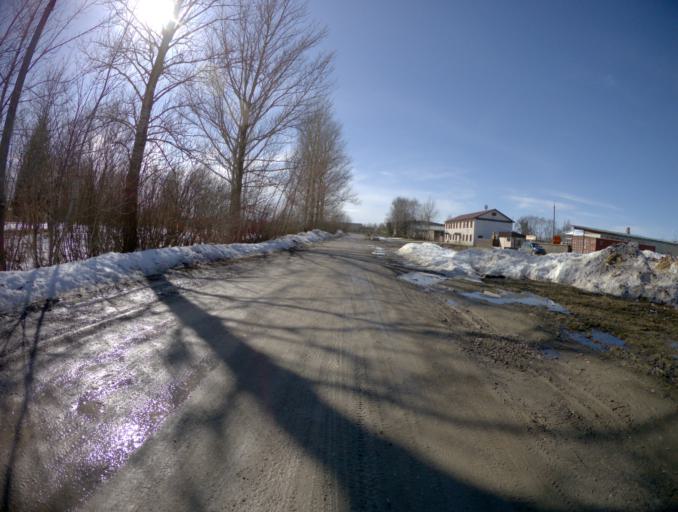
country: RU
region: Vladimir
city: Suzdal'
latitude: 56.4429
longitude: 40.4566
